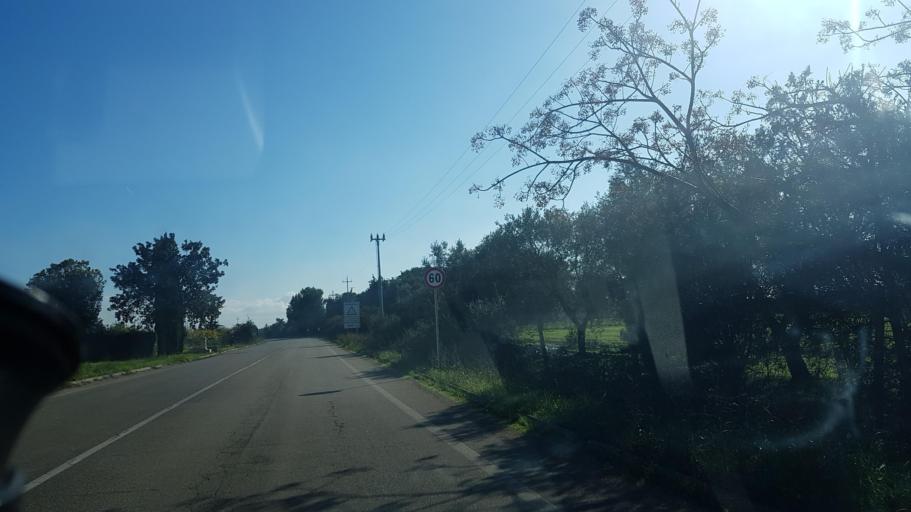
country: IT
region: Apulia
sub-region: Provincia di Lecce
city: Novoli
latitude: 40.3818
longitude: 18.0303
